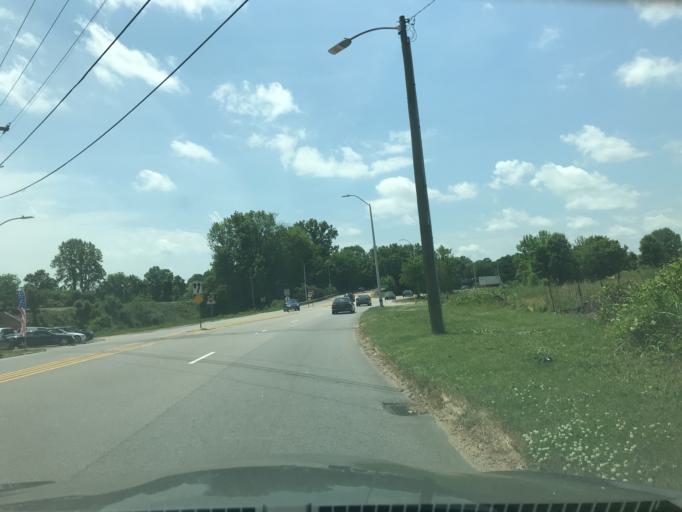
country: US
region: North Carolina
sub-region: Wake County
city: Raleigh
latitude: 35.8044
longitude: -78.6253
